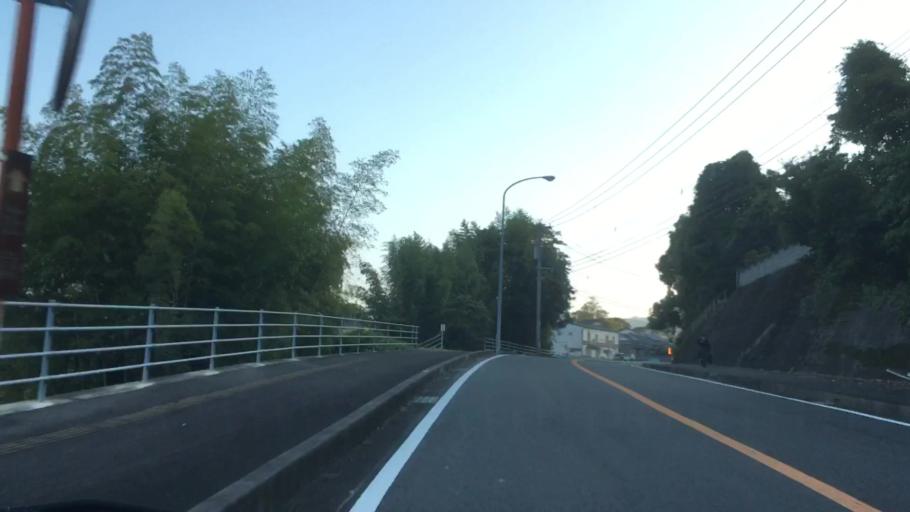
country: JP
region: Nagasaki
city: Sasebo
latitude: 33.0067
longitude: 129.7312
